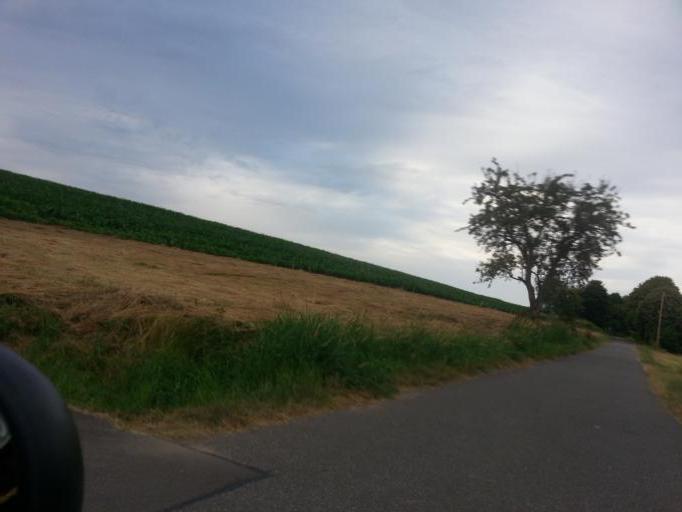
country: DE
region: Rheinland-Pfalz
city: Gimbweiler
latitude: 49.5729
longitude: 7.1719
